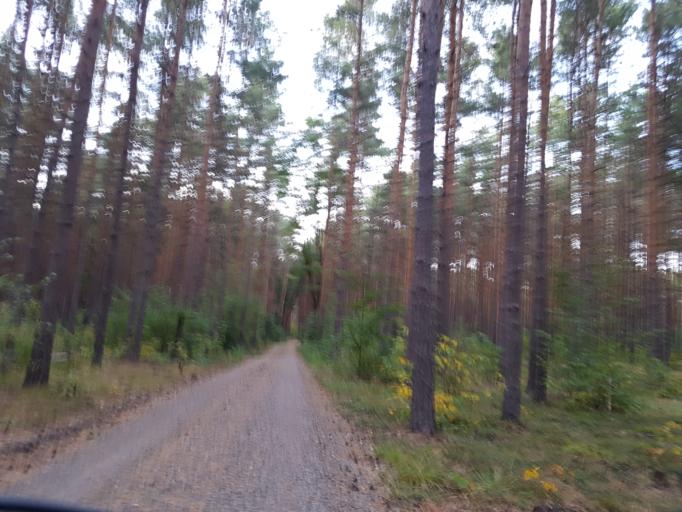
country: DE
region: Brandenburg
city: Trobitz
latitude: 51.5770
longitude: 13.4591
